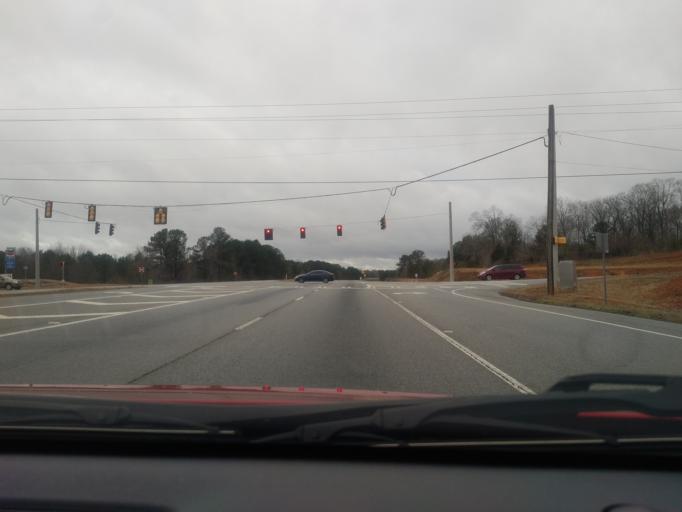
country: US
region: Georgia
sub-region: Spalding County
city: East Griffin
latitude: 33.2406
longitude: -84.1645
